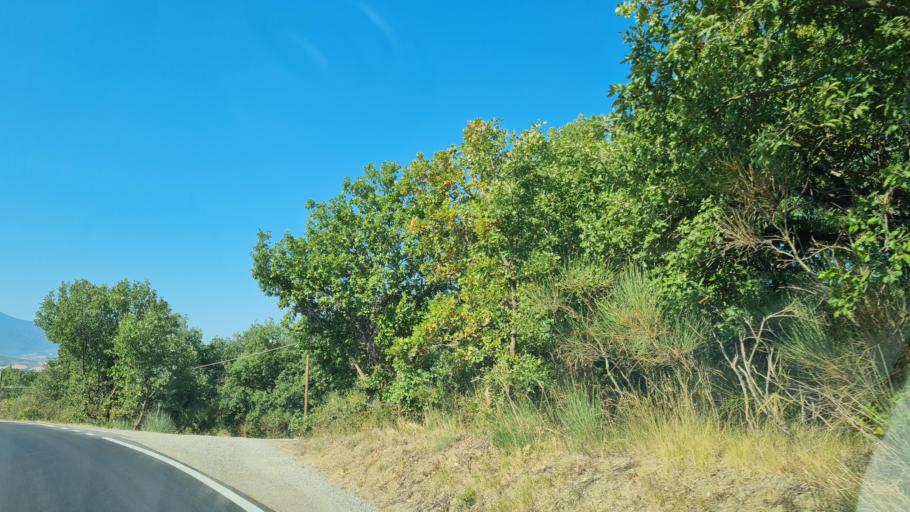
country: IT
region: Tuscany
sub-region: Provincia di Siena
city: Chianciano Terme
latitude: 43.0174
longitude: 11.7659
